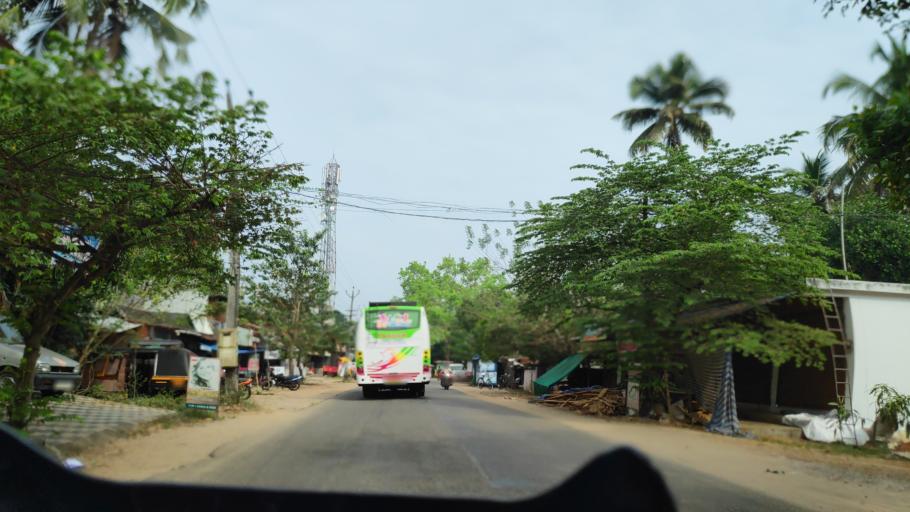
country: IN
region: Kerala
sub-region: Alappuzha
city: Kutiatodu
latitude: 9.8154
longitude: 76.3514
